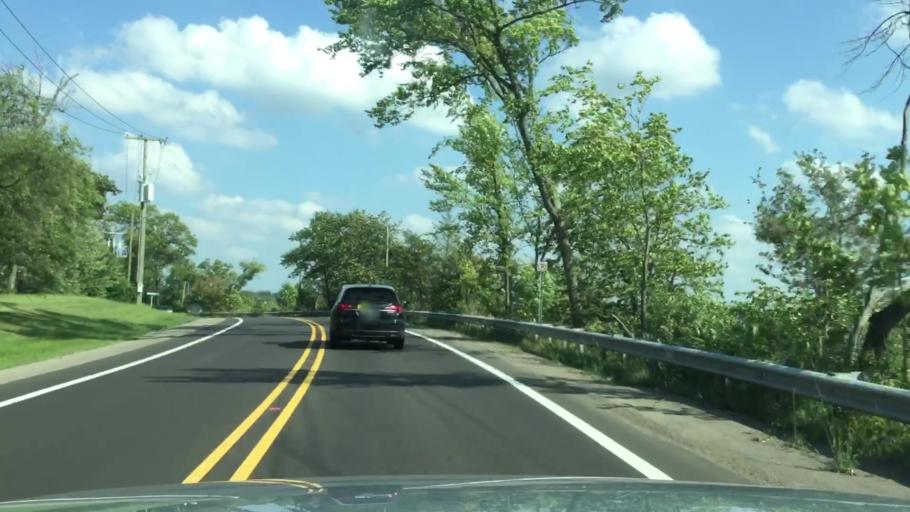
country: US
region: Michigan
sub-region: Oakland County
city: Orchard Lake
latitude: 42.5961
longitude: -83.3701
